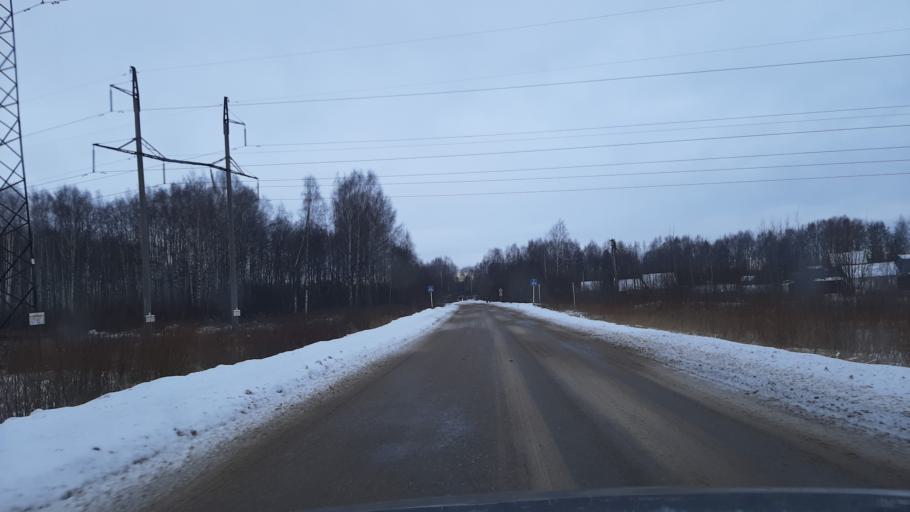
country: RU
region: Kostroma
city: Volgorechensk
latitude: 57.4447
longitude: 41.1379
